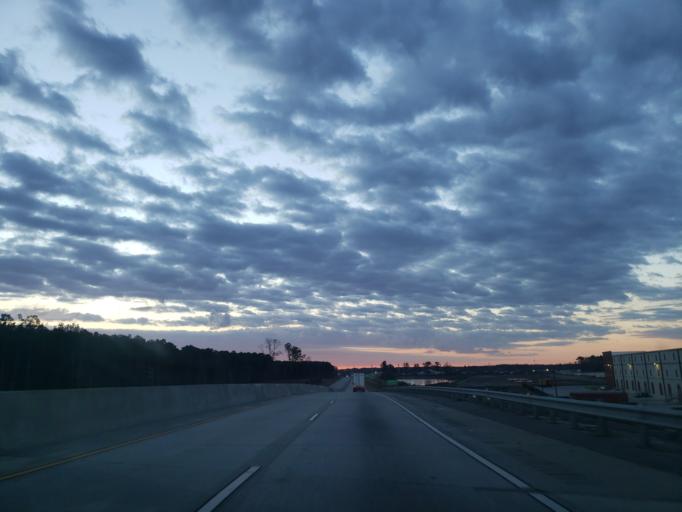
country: US
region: Georgia
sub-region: Chatham County
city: Port Wentworth
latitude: 32.1471
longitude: -81.1732
